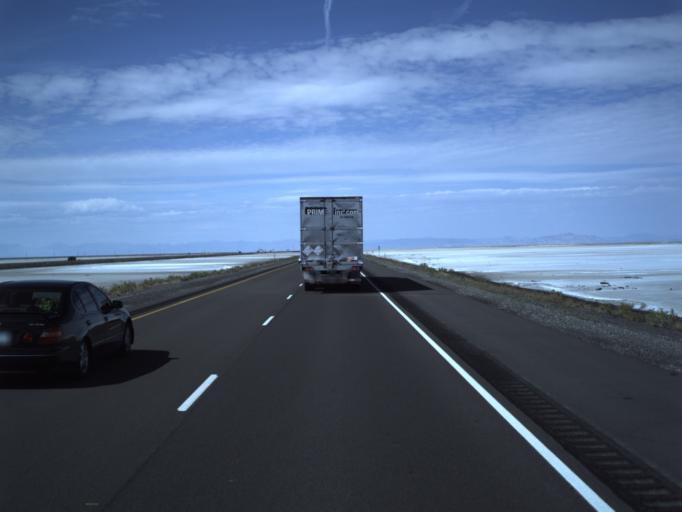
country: US
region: Utah
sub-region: Tooele County
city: Wendover
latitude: 40.7302
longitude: -113.4333
